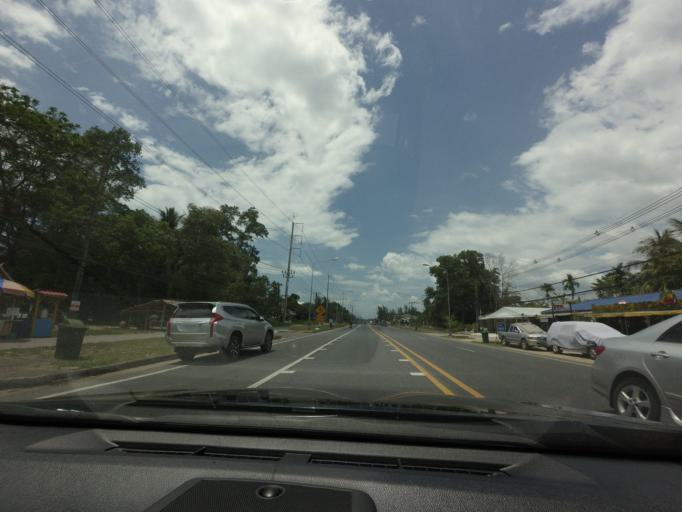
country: TH
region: Phangnga
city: Ban Khao Lak
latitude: 8.6567
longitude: 98.2534
